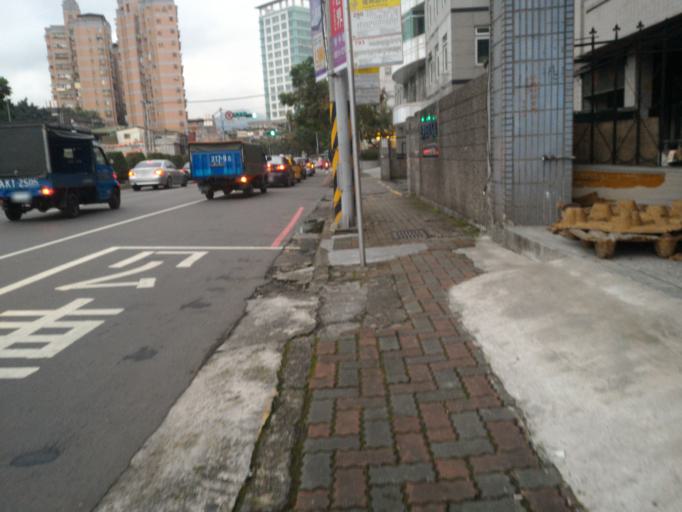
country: TW
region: Taipei
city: Taipei
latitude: 24.9871
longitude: 121.5367
